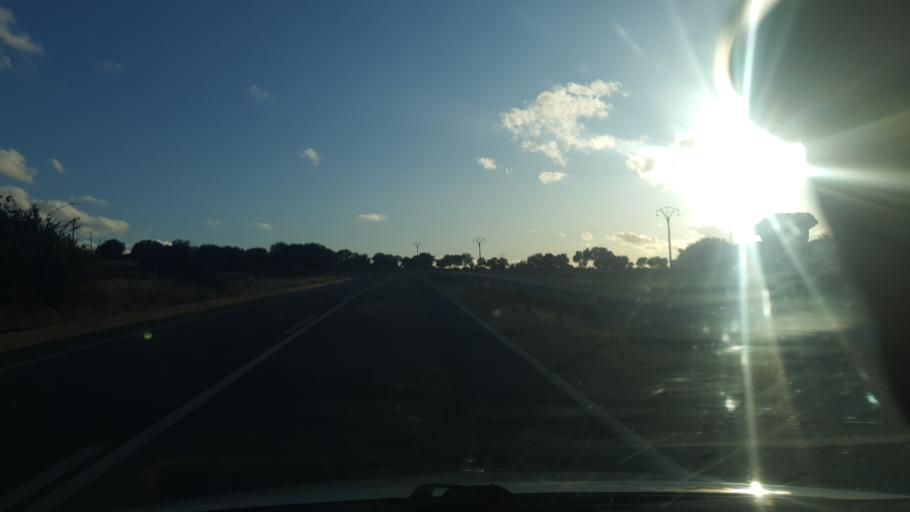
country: ES
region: Castille and Leon
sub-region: Provincia de Avila
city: Mingorria
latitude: 40.7393
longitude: -4.6738
